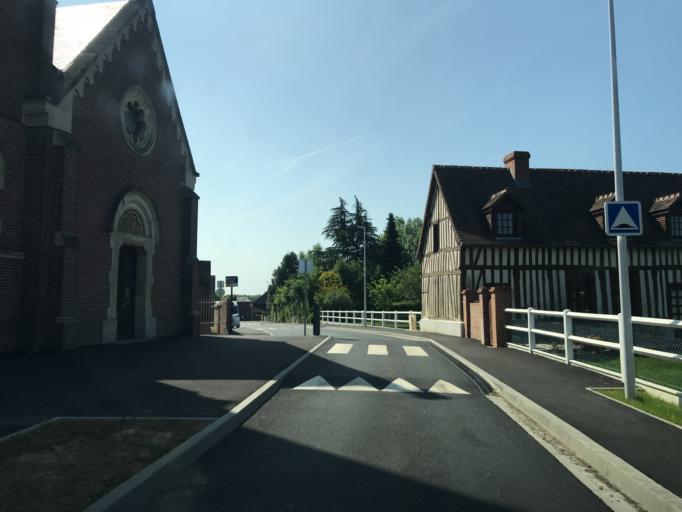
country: FR
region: Haute-Normandie
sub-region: Departement de la Seine-Maritime
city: Ymare
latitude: 49.3663
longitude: 1.1585
